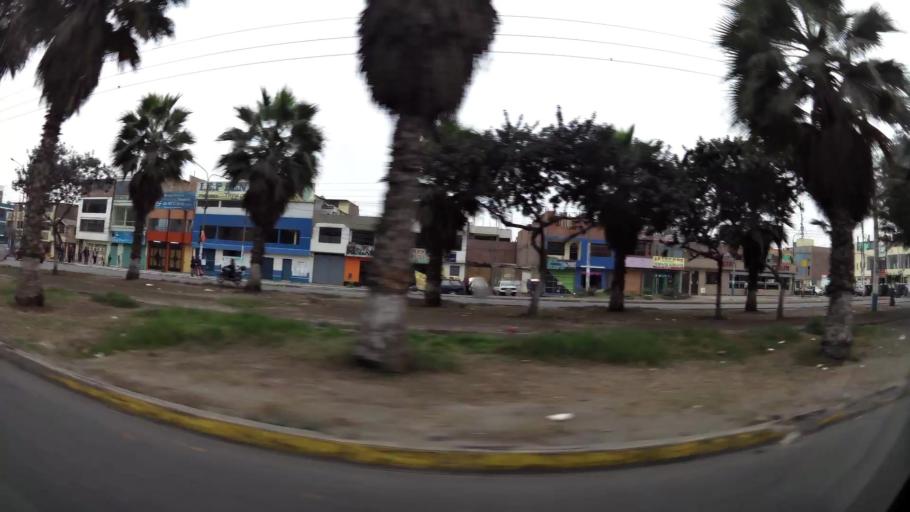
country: PE
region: Lima
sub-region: Lima
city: Urb. Santo Domingo
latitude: -11.9301
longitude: -77.0536
